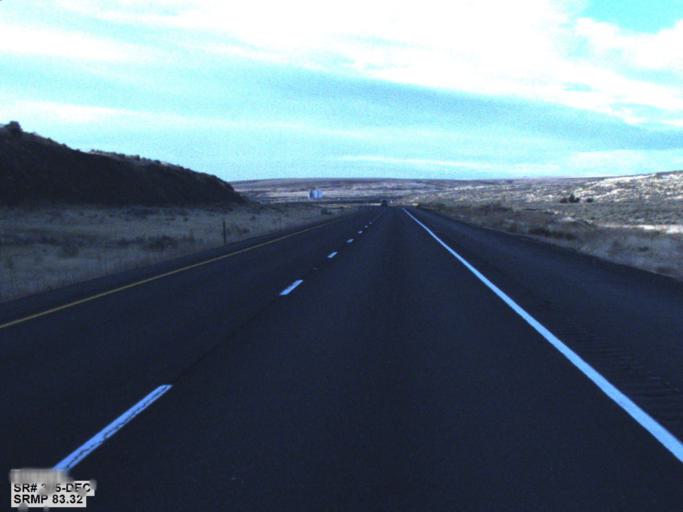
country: US
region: Washington
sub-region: Adams County
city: Ritzville
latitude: 46.9855
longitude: -118.5592
